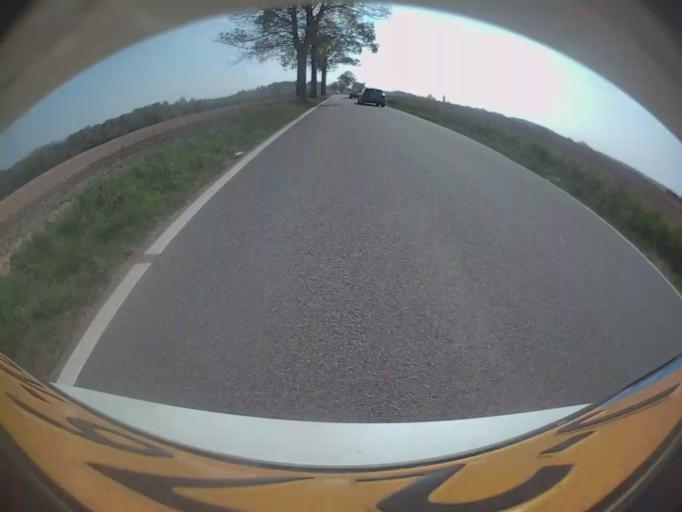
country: BE
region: Wallonia
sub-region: Province de Namur
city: Havelange
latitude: 50.3217
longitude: 5.2458
